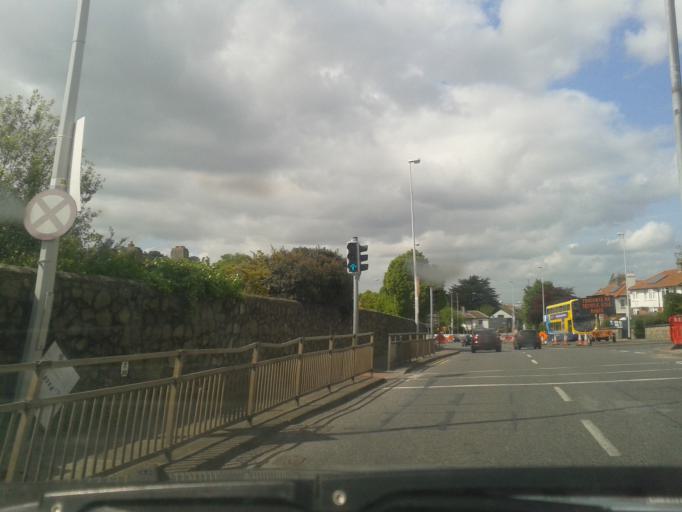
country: IE
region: Leinster
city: Blackrock
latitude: 53.2959
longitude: -6.1700
